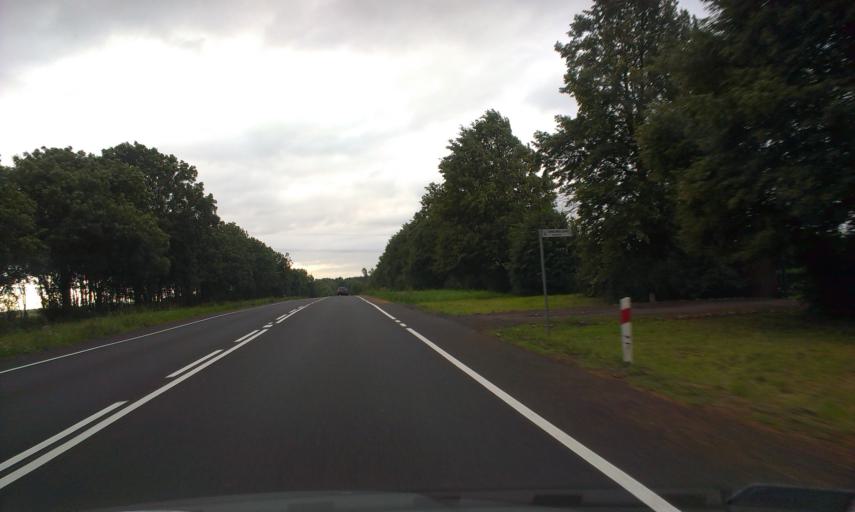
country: PL
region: Greater Poland Voivodeship
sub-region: Powiat pilski
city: Ujscie
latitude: 53.0360
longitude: 16.7751
